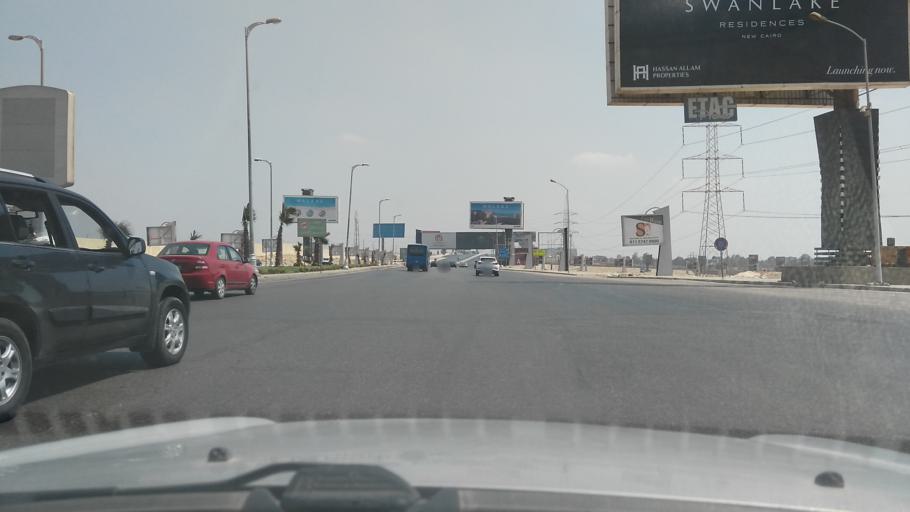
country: EG
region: Al Jizah
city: Awsim
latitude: 30.0430
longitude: 31.0459
